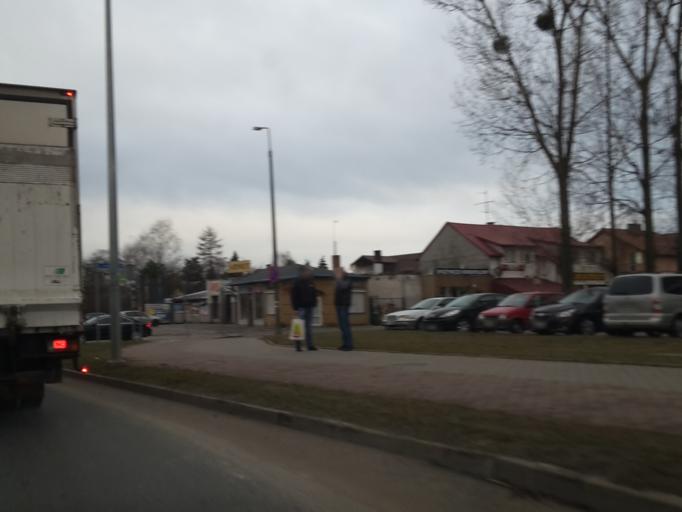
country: PL
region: Warmian-Masurian Voivodeship
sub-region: Powiat elblaski
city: Elblag
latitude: 54.1779
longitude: 19.4229
